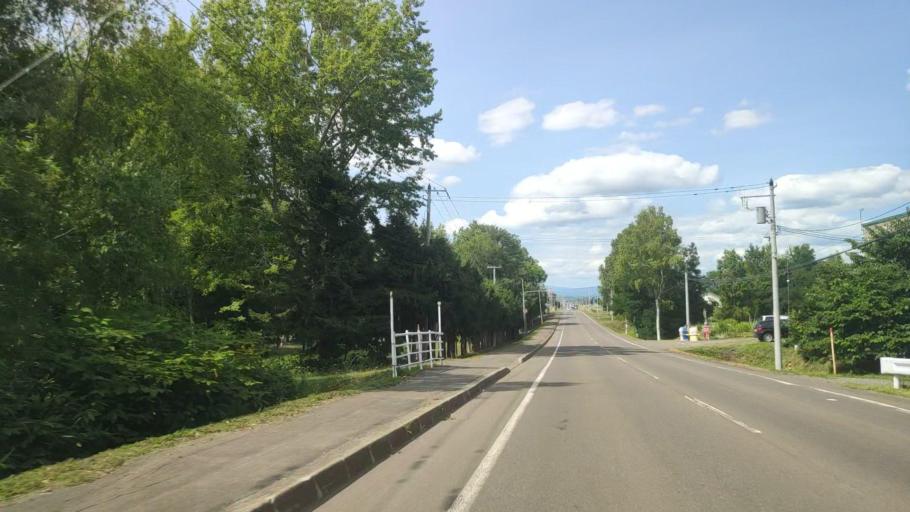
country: JP
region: Hokkaido
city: Nayoro
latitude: 44.2867
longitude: 142.4295
